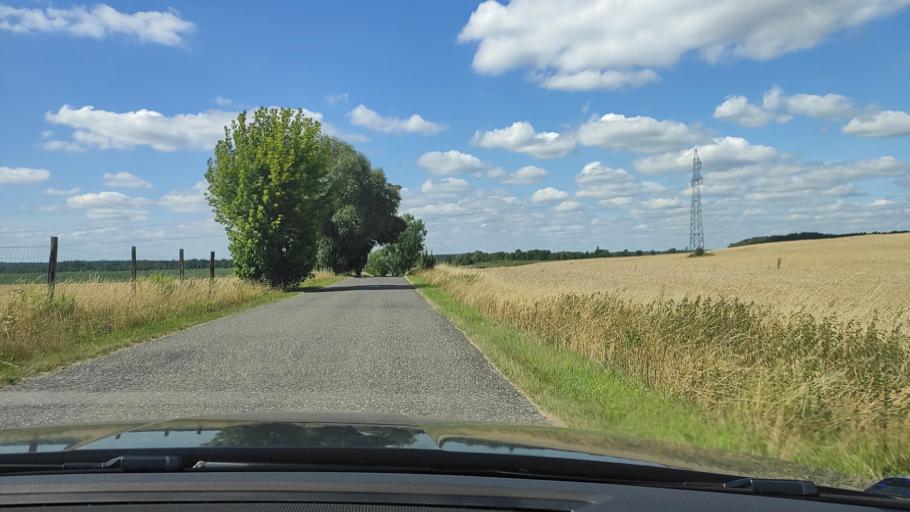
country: PL
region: Greater Poland Voivodeship
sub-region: Powiat poznanski
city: Kobylnica
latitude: 52.4886
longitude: 17.1338
